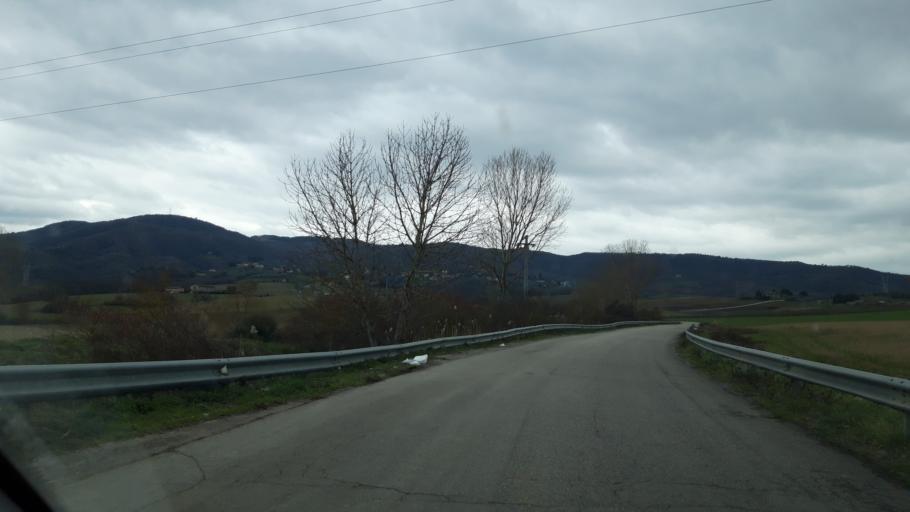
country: IT
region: Umbria
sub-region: Provincia di Perugia
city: Fontignano
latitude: 42.9923
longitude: 12.1863
